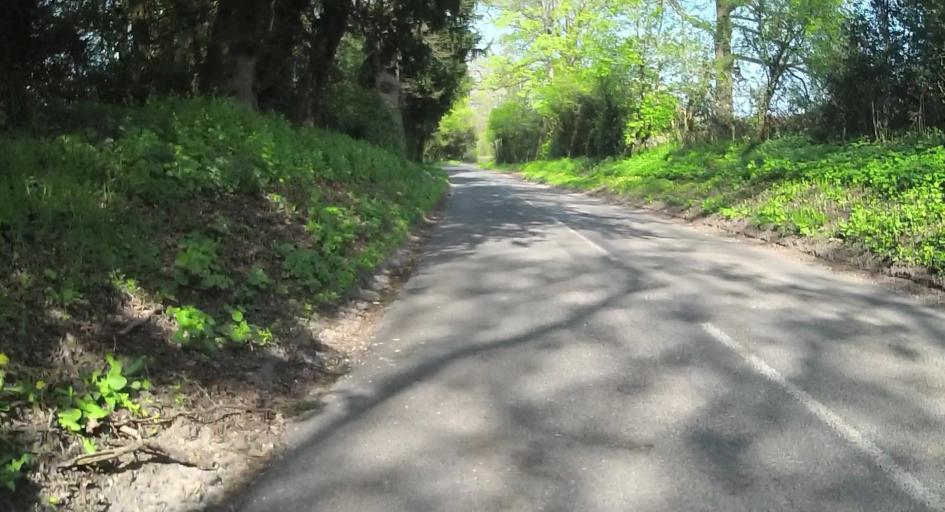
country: GB
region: England
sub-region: Hampshire
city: Basingstoke
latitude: 51.3035
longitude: -1.0886
